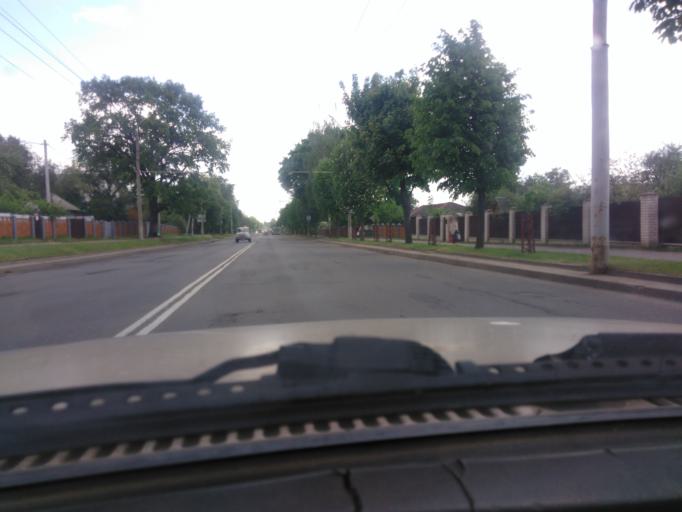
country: BY
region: Mogilev
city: Mahilyow
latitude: 53.9310
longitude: 30.3373
